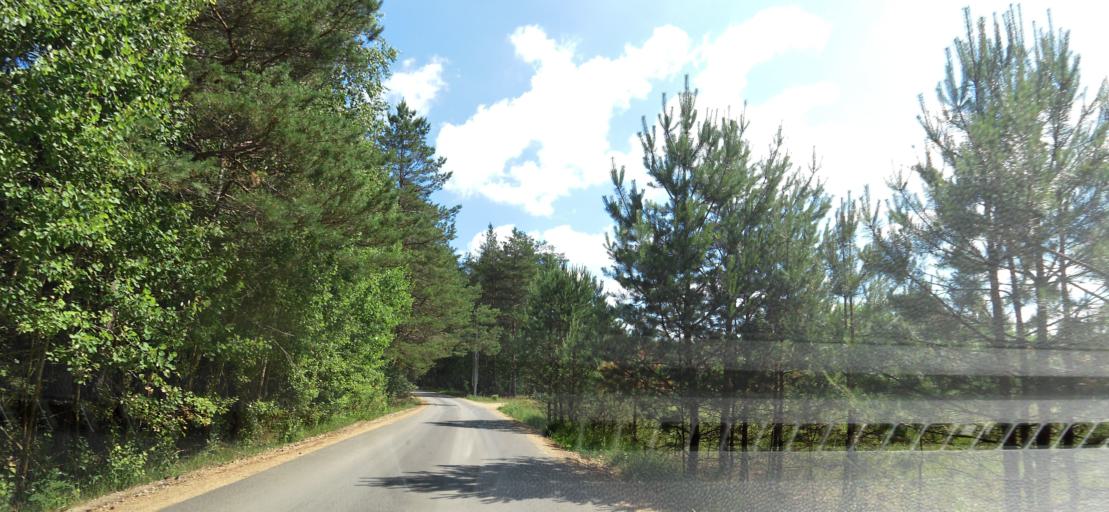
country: LT
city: Nemencine
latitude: 54.8223
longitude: 25.4068
